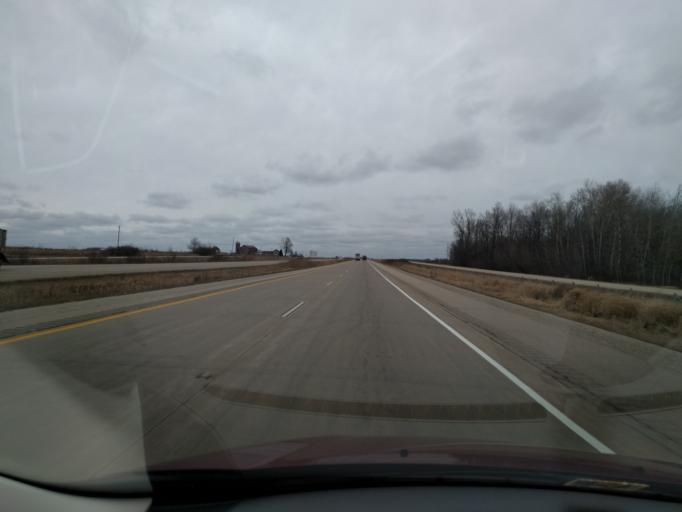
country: US
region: Wisconsin
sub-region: Winnebago County
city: Winneconne
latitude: 44.2305
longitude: -88.7183
